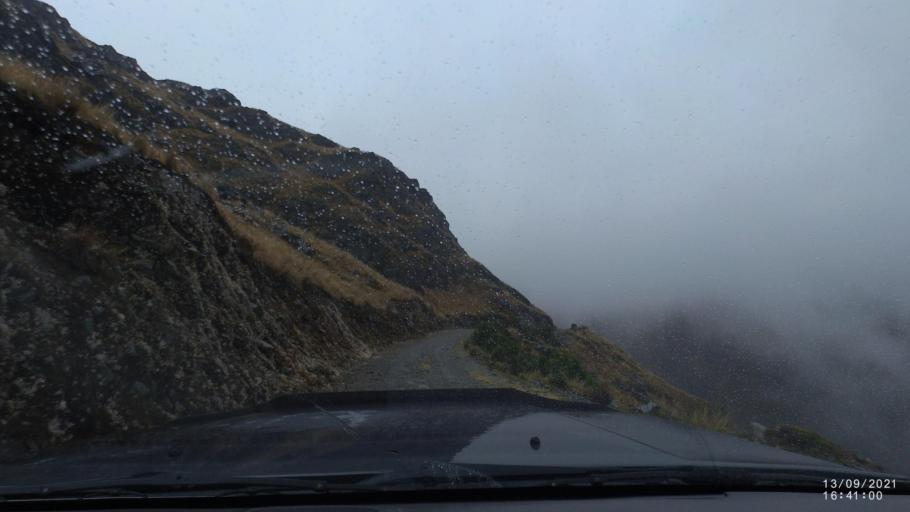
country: BO
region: Cochabamba
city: Colomi
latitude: -17.2832
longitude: -65.7107
